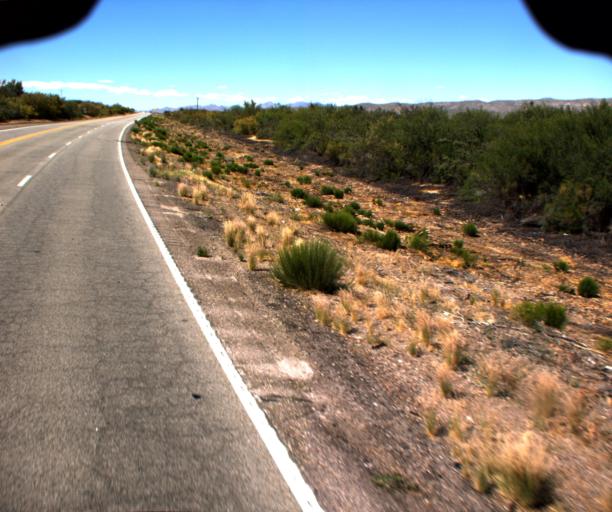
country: US
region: Arizona
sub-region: Yavapai County
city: Bagdad
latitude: 34.8024
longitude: -113.6258
